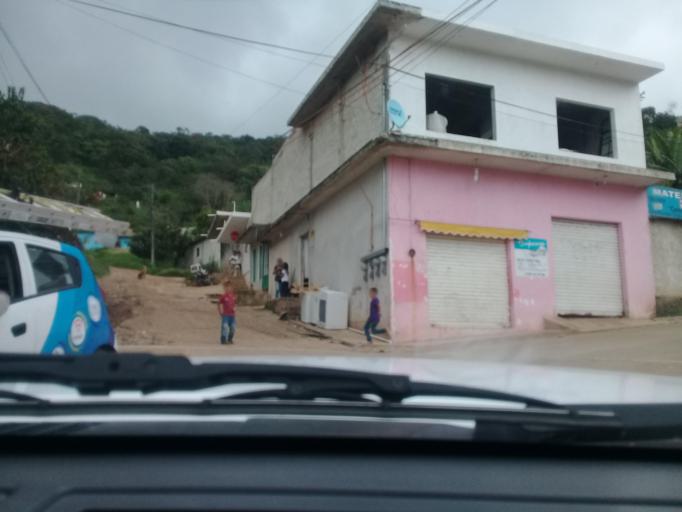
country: MX
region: Veracruz
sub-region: Tlalnelhuayocan
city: Guadalupe Victoria
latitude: 19.5579
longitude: -96.9565
